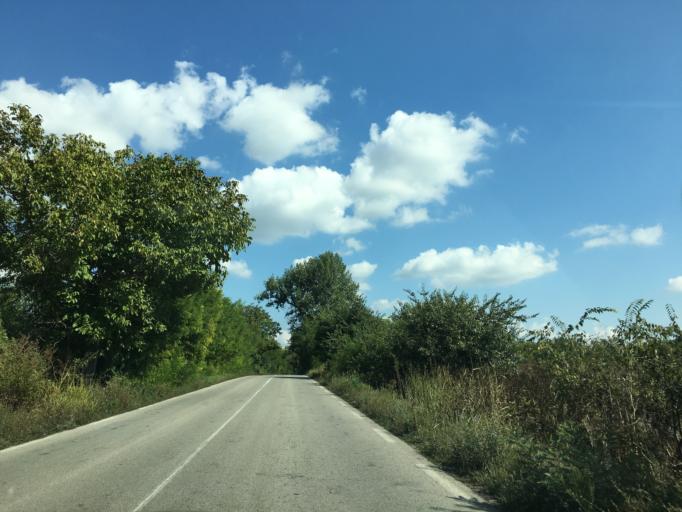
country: BG
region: Montana
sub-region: Obshtina Lom
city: Lom
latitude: 43.8169
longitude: 23.1871
